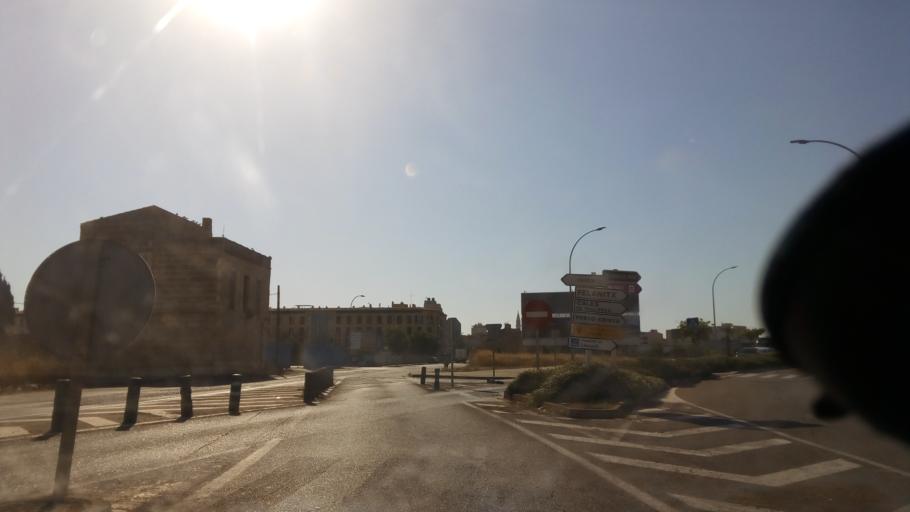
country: ES
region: Balearic Islands
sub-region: Illes Balears
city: Manacor
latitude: 39.5719
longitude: 3.1962
